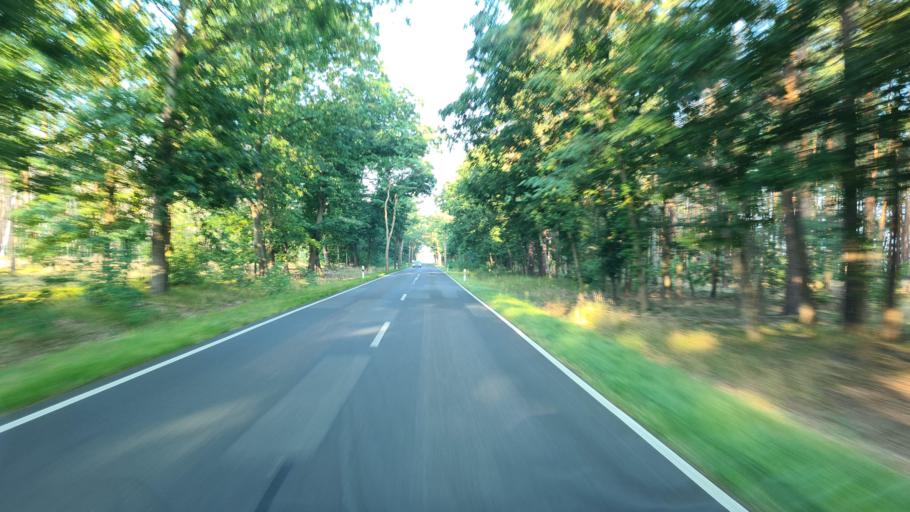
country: DE
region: Brandenburg
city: Juterbog
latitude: 52.0942
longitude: 13.0424
